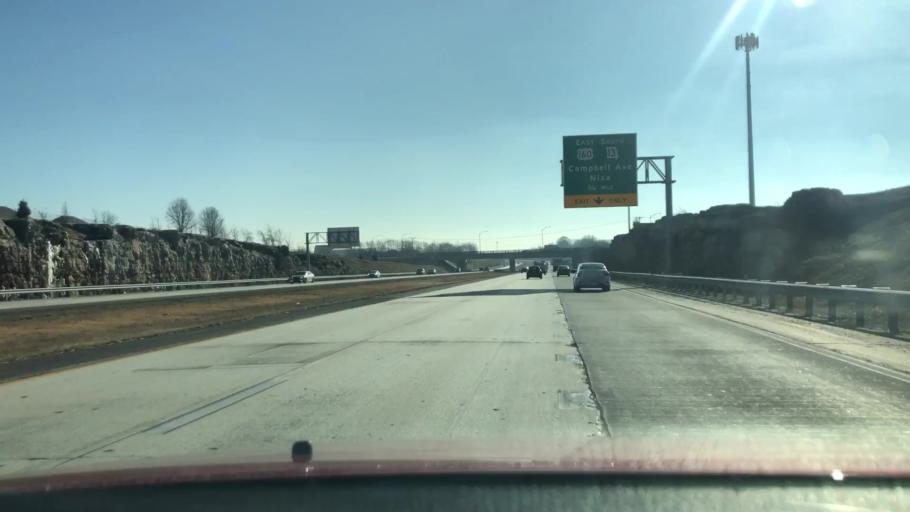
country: US
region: Missouri
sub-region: Greene County
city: Battlefield
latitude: 37.1402
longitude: -93.3141
